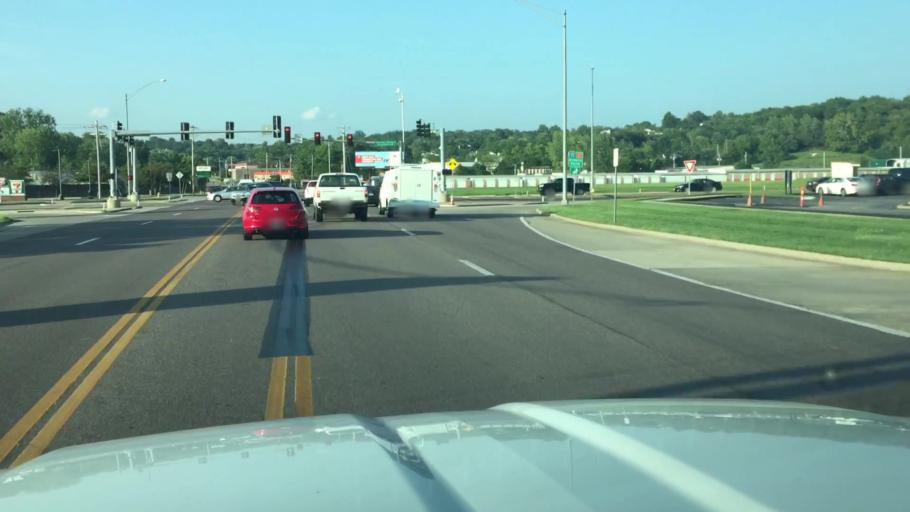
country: US
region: Missouri
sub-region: Jefferson County
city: Arnold
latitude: 38.4641
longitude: -90.3575
